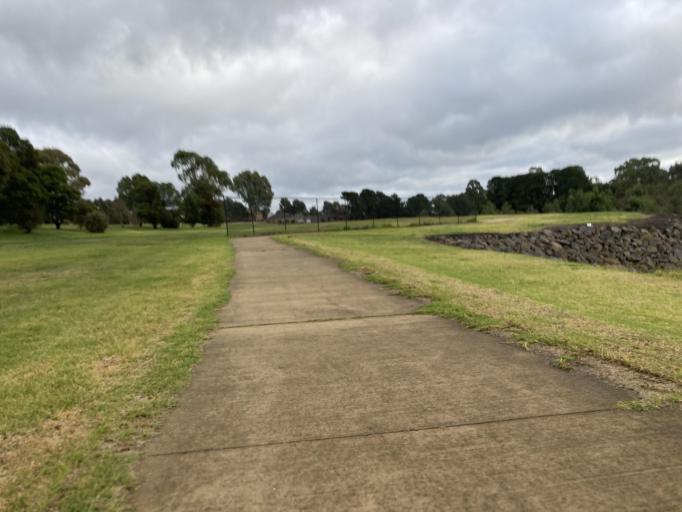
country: AU
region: Victoria
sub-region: Hume
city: Roxburgh Park
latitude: -37.6003
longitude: 144.9193
